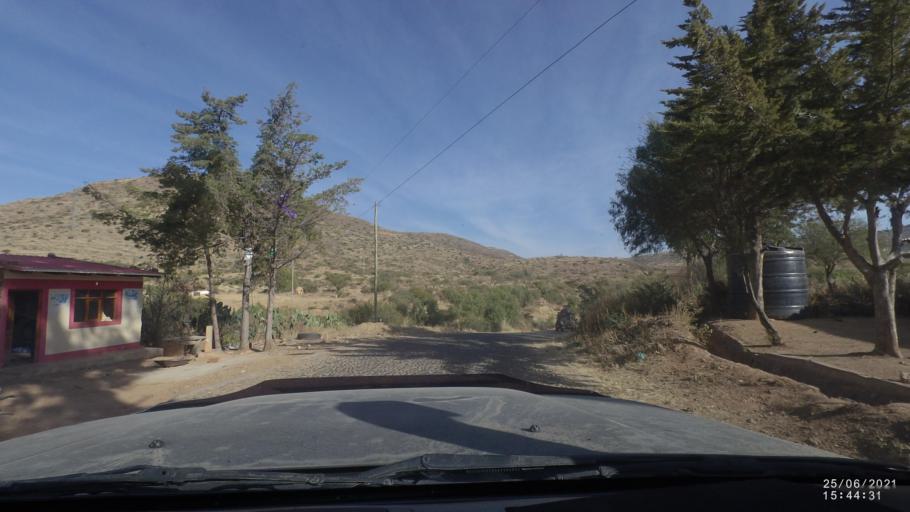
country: BO
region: Cochabamba
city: Cliza
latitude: -17.6571
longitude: -65.9107
